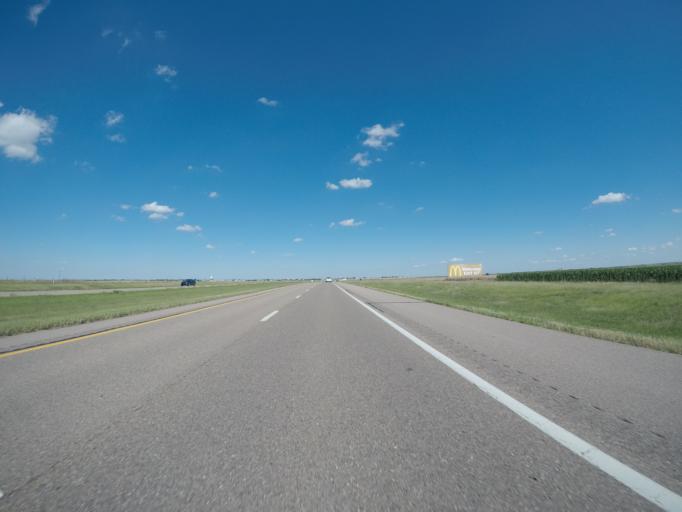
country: US
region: Kansas
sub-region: Trego County
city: WaKeeney
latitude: 39.0204
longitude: -99.9188
